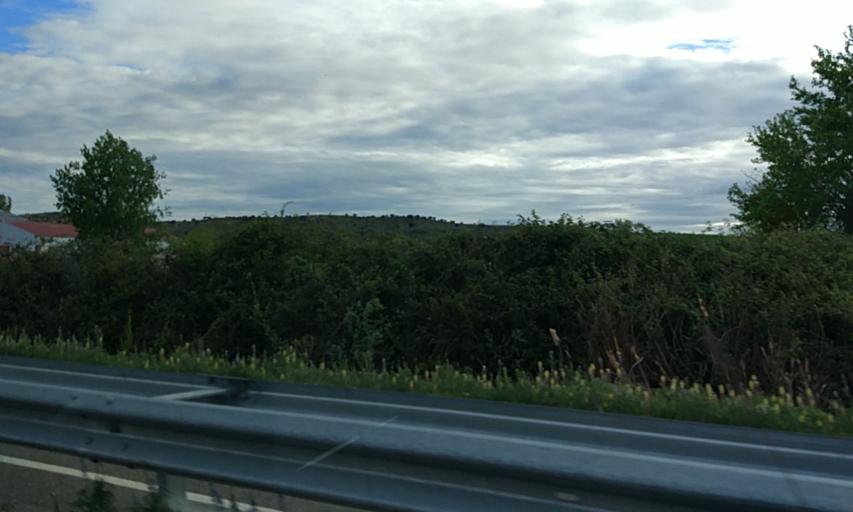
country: ES
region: Extremadura
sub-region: Provincia de Caceres
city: Coria
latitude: 39.9653
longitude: -6.5183
